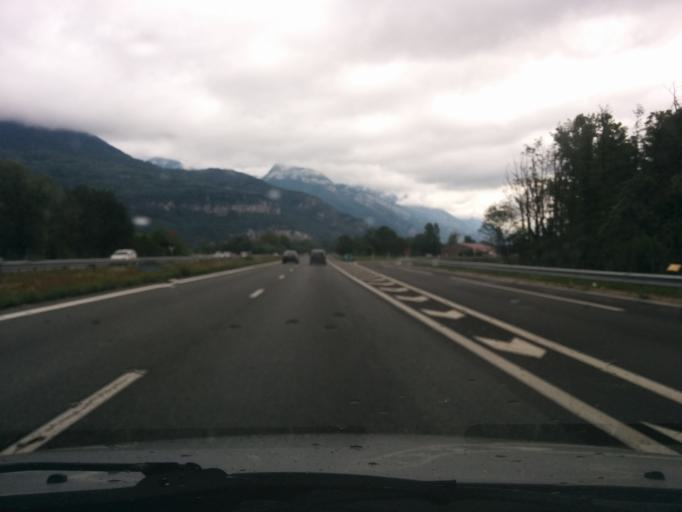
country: FR
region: Rhone-Alpes
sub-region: Departement de l'Isere
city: Saint-Jean-de-Moirans
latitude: 45.3255
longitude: 5.5990
